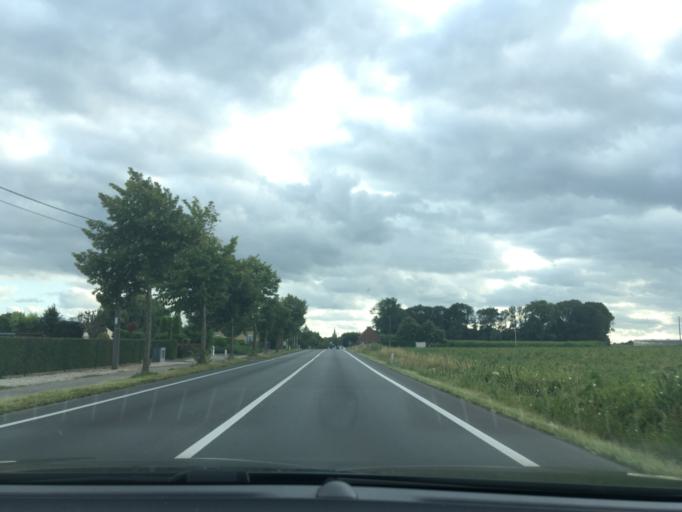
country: BE
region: Flanders
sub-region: Provincie West-Vlaanderen
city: Staden
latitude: 50.9399
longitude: 3.0249
